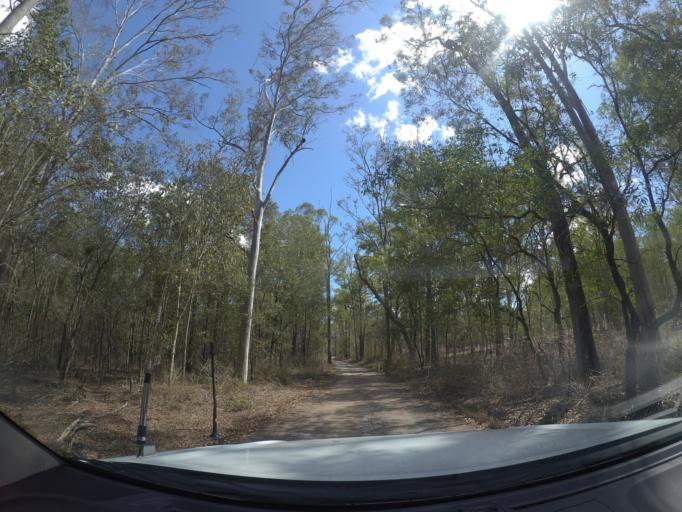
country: AU
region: Queensland
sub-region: Logan
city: North Maclean
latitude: -27.8217
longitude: 152.9692
